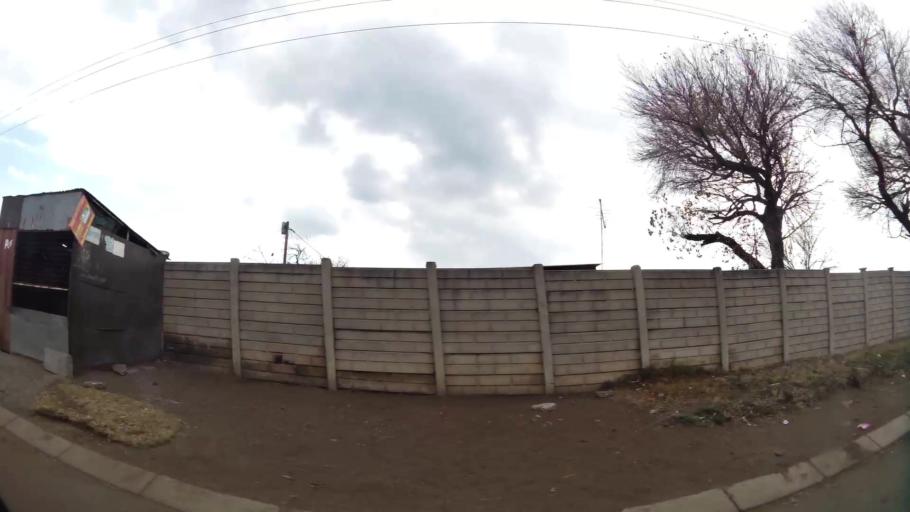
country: ZA
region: Gauteng
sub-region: Sedibeng District Municipality
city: Vanderbijlpark
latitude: -26.6650
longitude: 27.8460
